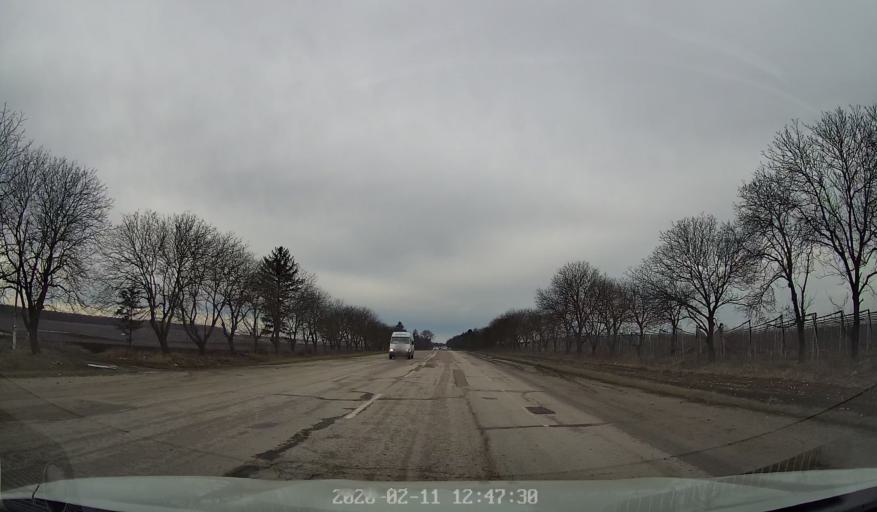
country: MD
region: Briceni
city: Briceni
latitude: 48.2724
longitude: 27.1628
